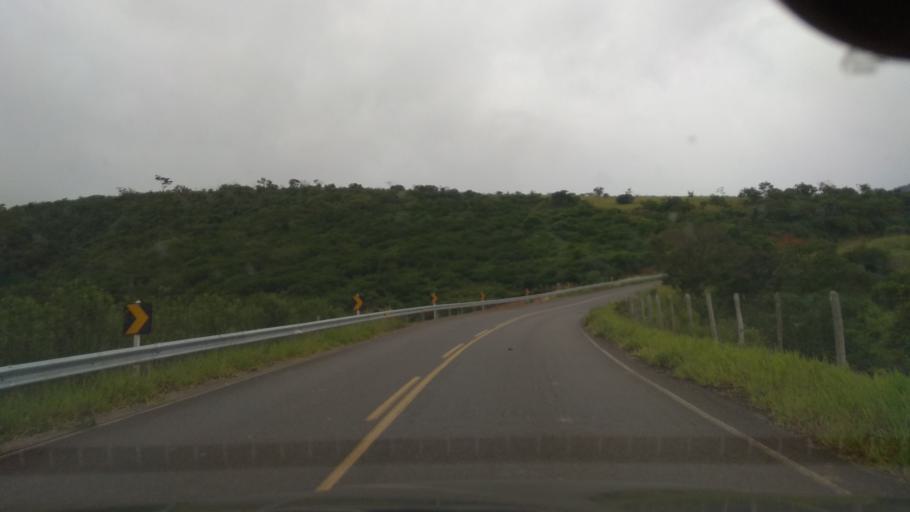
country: BR
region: Bahia
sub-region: Santa Ines
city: Santa Ines
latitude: -13.2388
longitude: -39.7514
